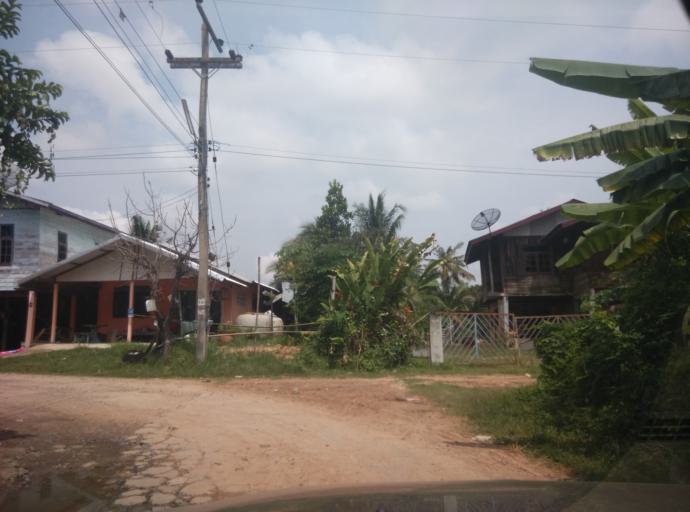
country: TH
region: Sisaket
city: Prang Ku
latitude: 14.9461
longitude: 104.0675
